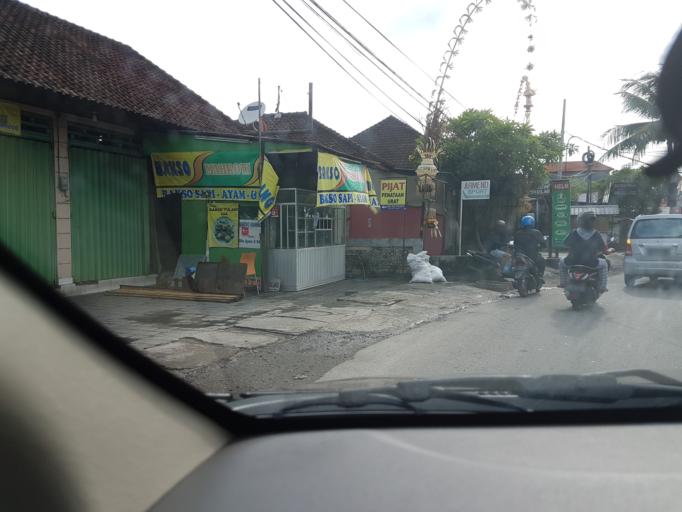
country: ID
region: Bali
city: Denpasar
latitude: -8.6731
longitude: 115.1821
